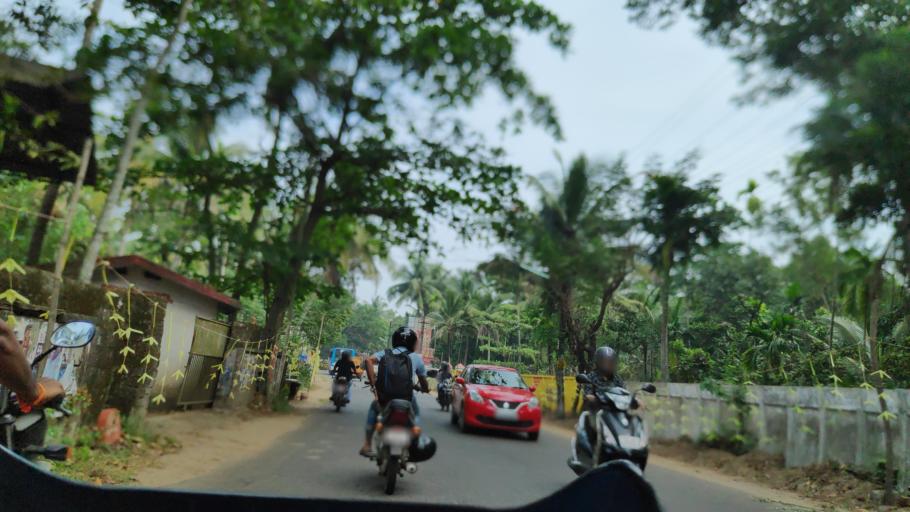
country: IN
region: Kerala
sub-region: Alappuzha
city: Shertallai
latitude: 9.7105
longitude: 76.3578
